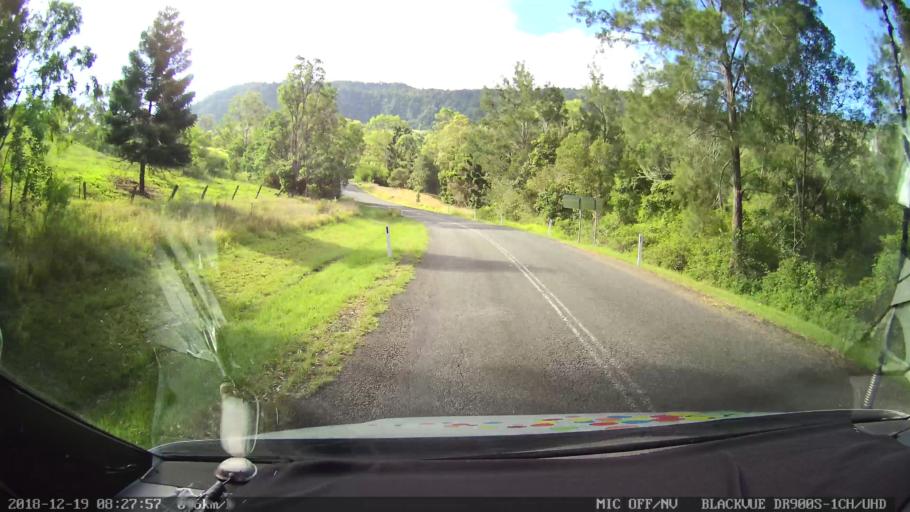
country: AU
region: New South Wales
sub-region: Kyogle
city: Kyogle
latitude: -28.3202
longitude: 152.9293
